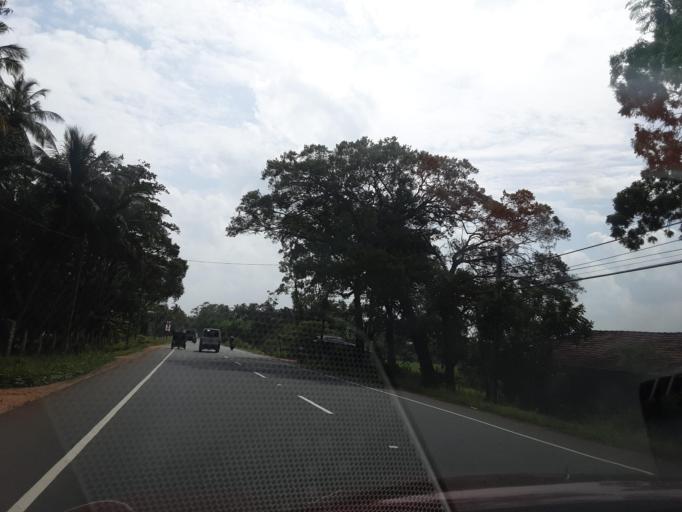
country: LK
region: North Central
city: Anuradhapura
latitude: 8.4997
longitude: 80.5122
